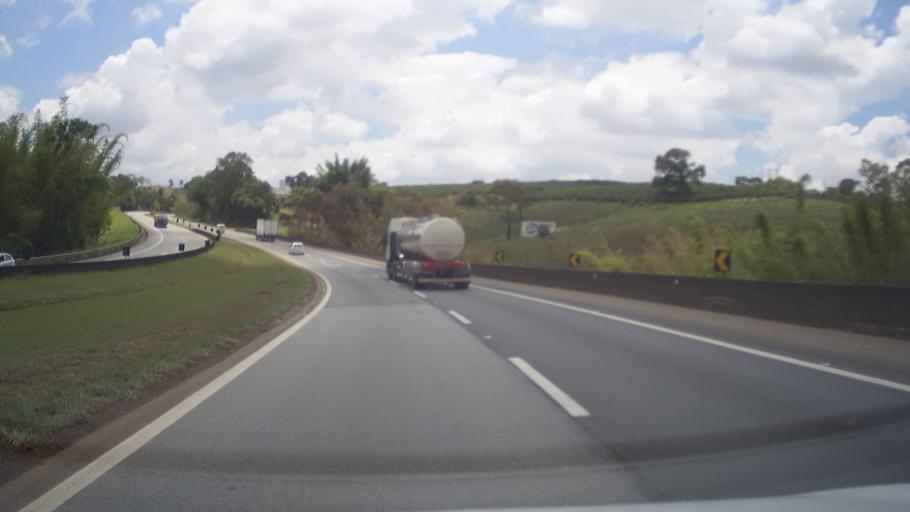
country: BR
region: Minas Gerais
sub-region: Tres Coracoes
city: Tres Coracoes
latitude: -21.7026
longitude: -45.3680
